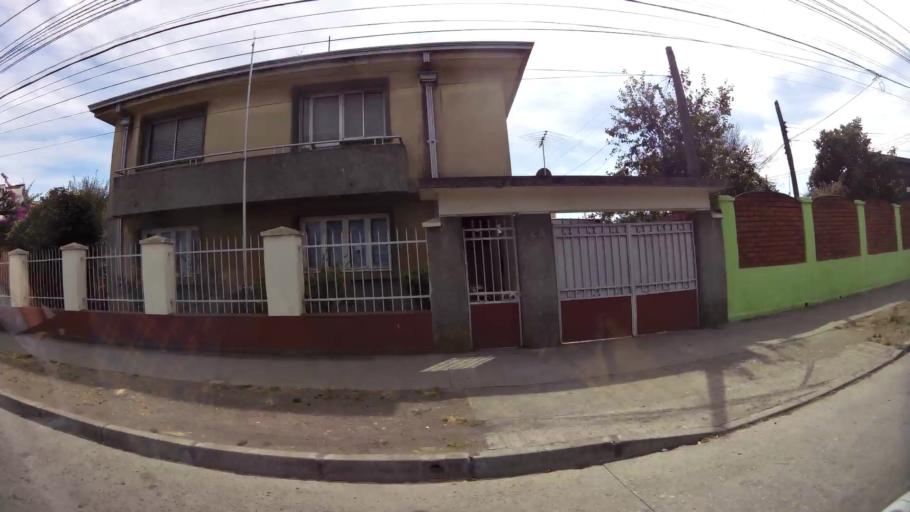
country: CL
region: Biobio
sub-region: Provincia de Concepcion
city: Talcahuano
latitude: -36.7238
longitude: -73.1201
